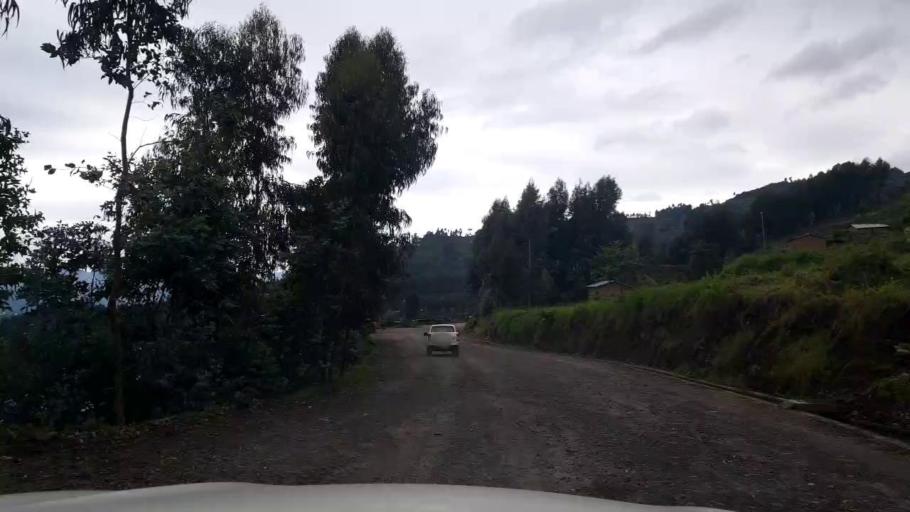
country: RW
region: Northern Province
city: Musanze
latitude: -1.5036
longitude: 29.5336
